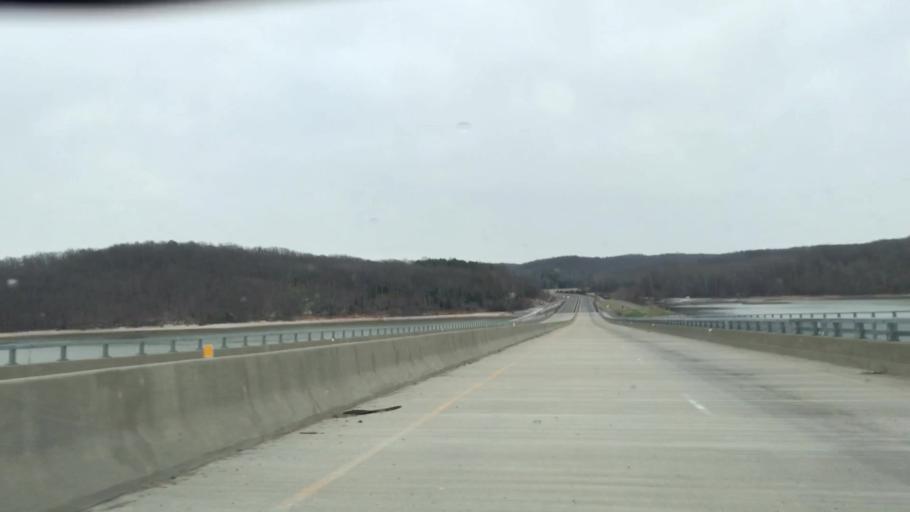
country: US
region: Kentucky
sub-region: Marshall County
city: Benton
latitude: 36.7730
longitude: -88.1184
